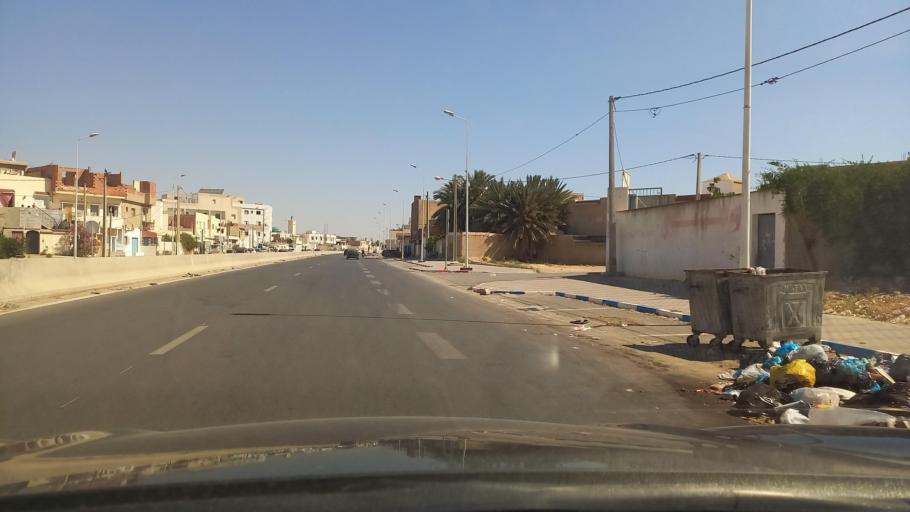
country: TN
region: Safaqis
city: Sfax
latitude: 34.7373
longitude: 10.7239
